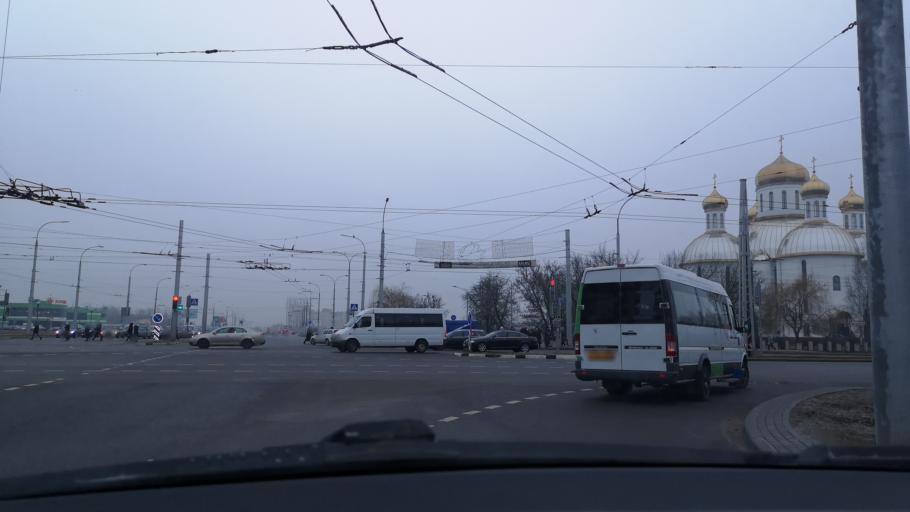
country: BY
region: Brest
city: Brest
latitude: 52.0999
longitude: 23.7636
